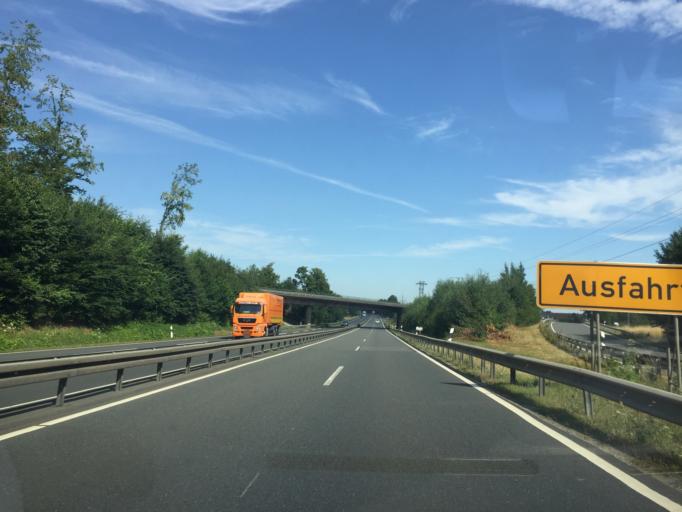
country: DE
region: Lower Saxony
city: Gittelde
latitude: 51.8422
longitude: 10.1790
